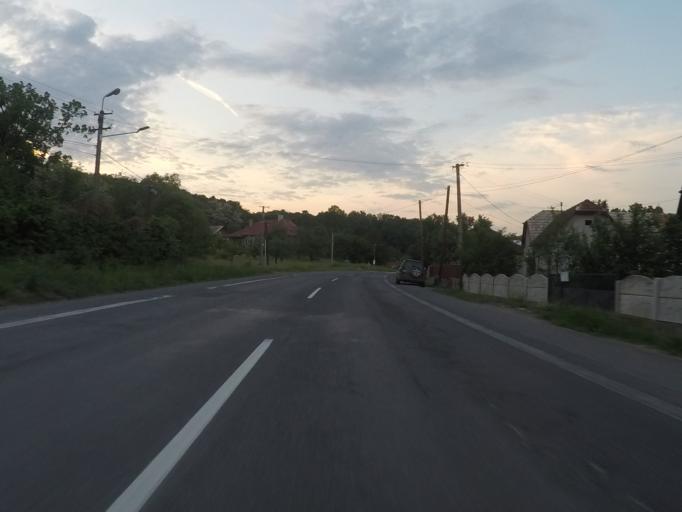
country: SK
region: Banskobystricky
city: Rimavska Sobota
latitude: 48.4706
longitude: 19.9500
